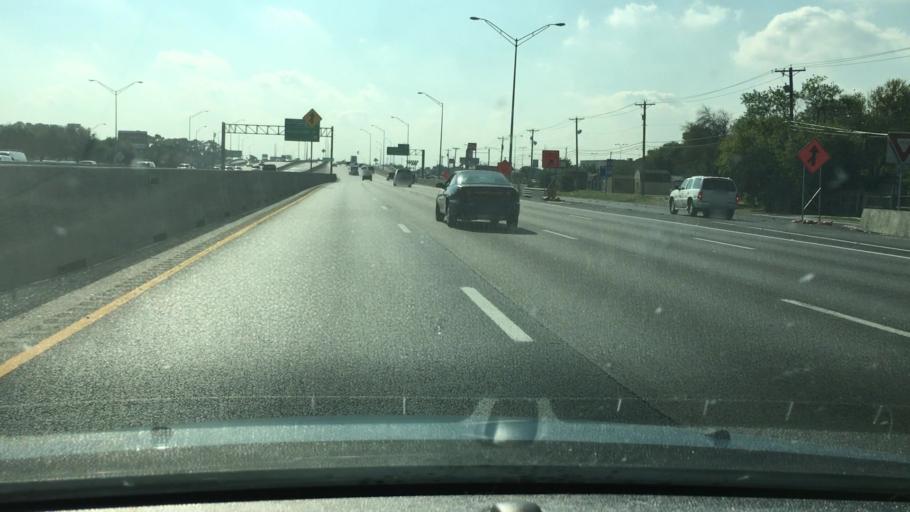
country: US
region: Texas
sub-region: Denton County
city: Lewisville
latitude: 33.0333
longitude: -96.9967
